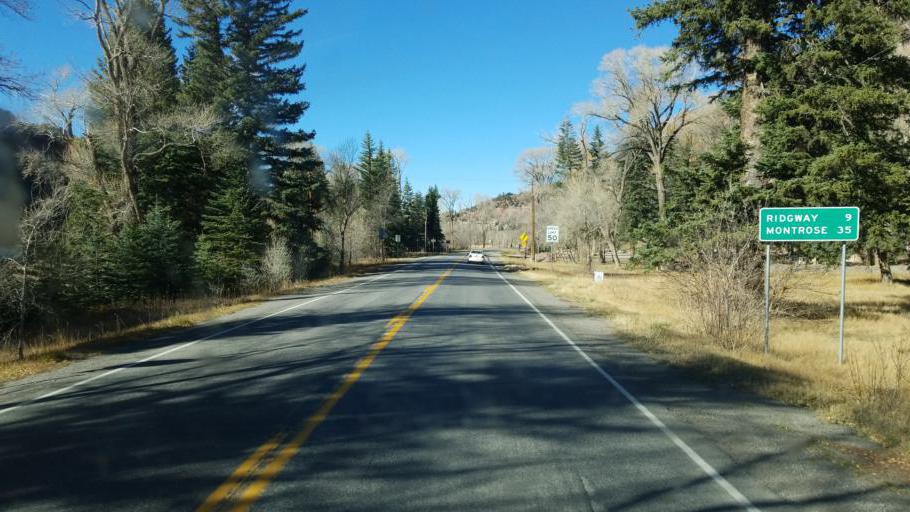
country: US
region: Colorado
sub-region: Ouray County
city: Ouray
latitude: 38.0425
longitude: -107.6809
